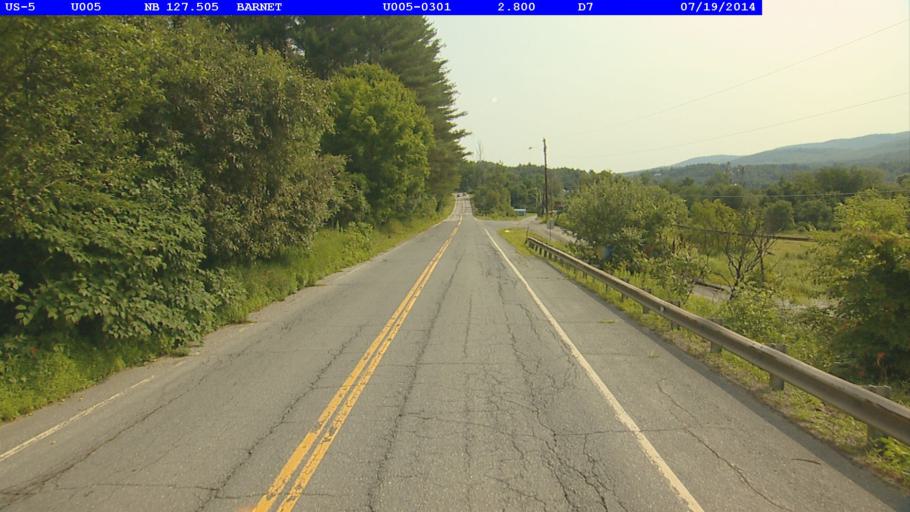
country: US
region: Vermont
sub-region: Caledonia County
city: Saint Johnsbury
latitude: 44.2923
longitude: -72.0555
